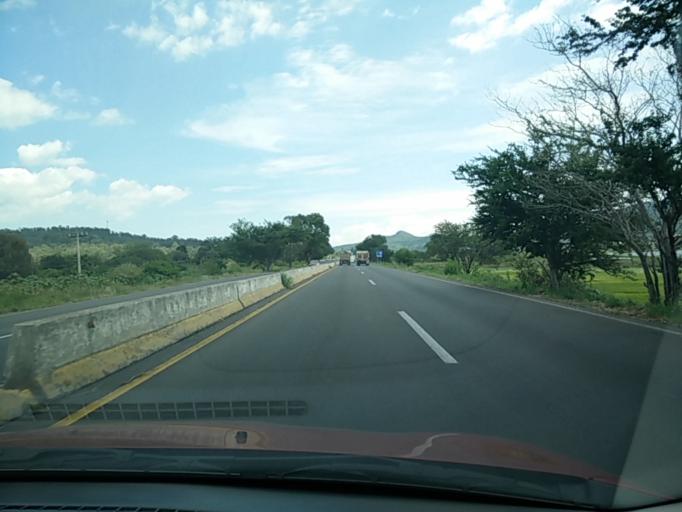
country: MX
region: Jalisco
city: Ixtlahuacan de los Membrillos
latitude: 20.3692
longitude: -103.2114
